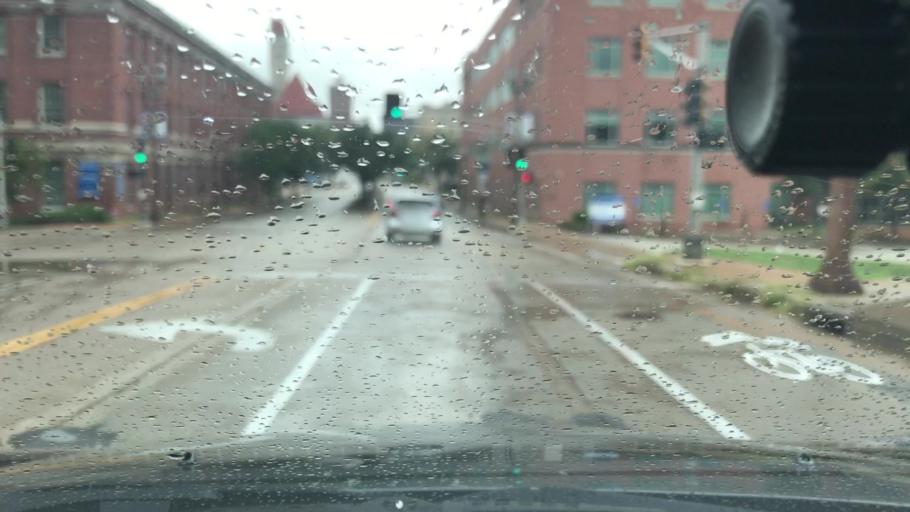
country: US
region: Missouri
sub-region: City of Saint Louis
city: St. Louis
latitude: 38.6256
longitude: -90.2074
